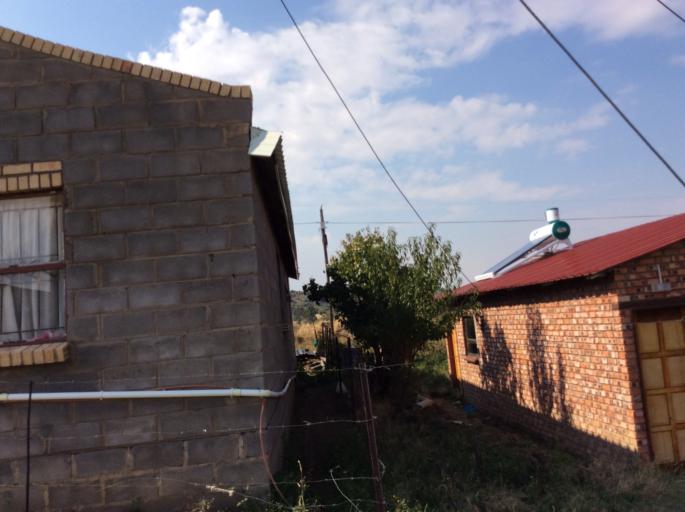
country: LS
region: Mafeteng
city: Mafeteng
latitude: -29.9827
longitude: 27.0100
